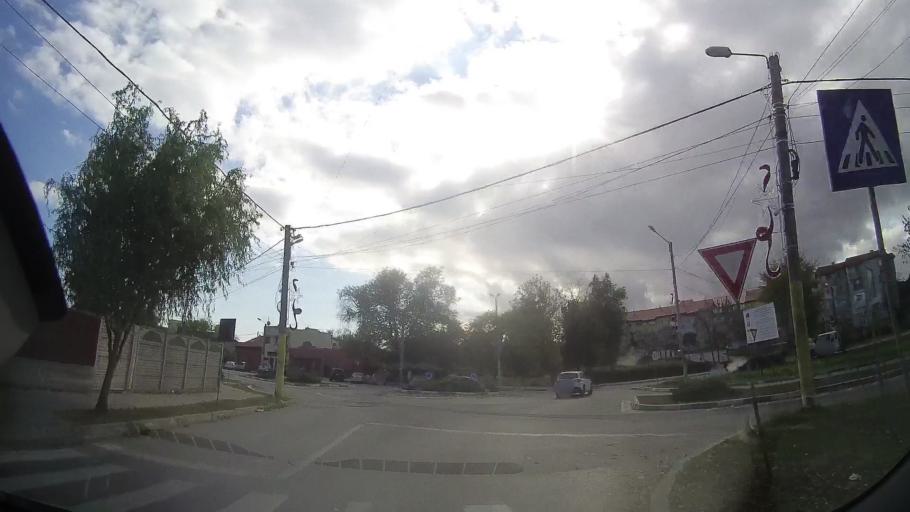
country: RO
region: Constanta
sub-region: Oras Techirghiol
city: Techirghiol
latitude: 44.0558
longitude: 28.6009
